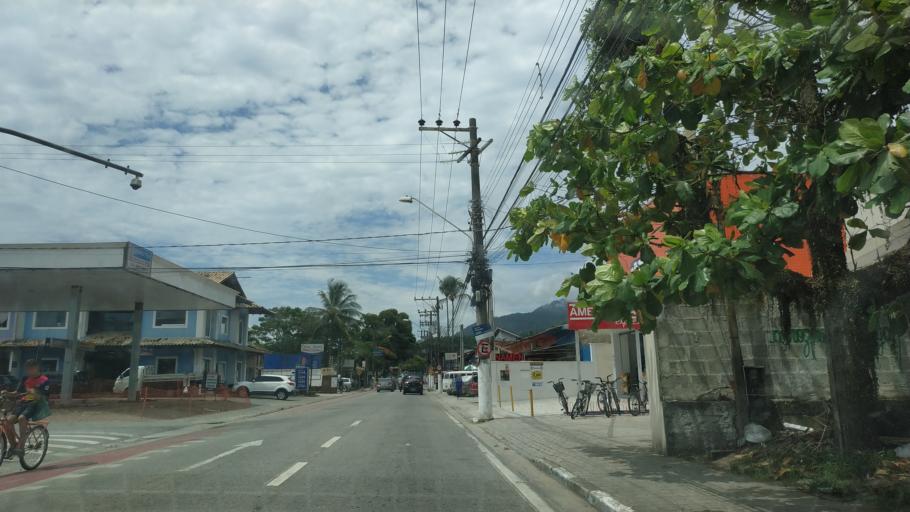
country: BR
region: Sao Paulo
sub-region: Ilhabela
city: Ilhabela
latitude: -23.8168
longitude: -45.3668
